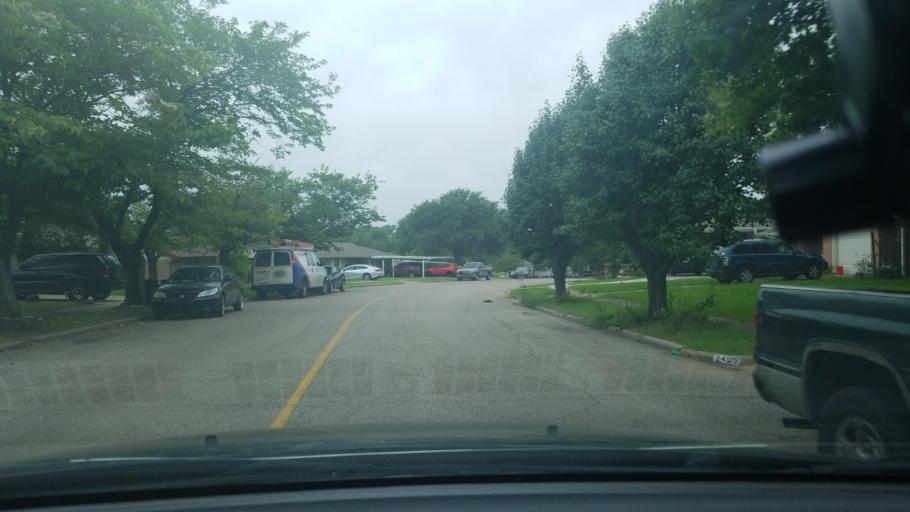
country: US
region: Texas
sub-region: Dallas County
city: Mesquite
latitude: 32.7883
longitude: -96.6332
